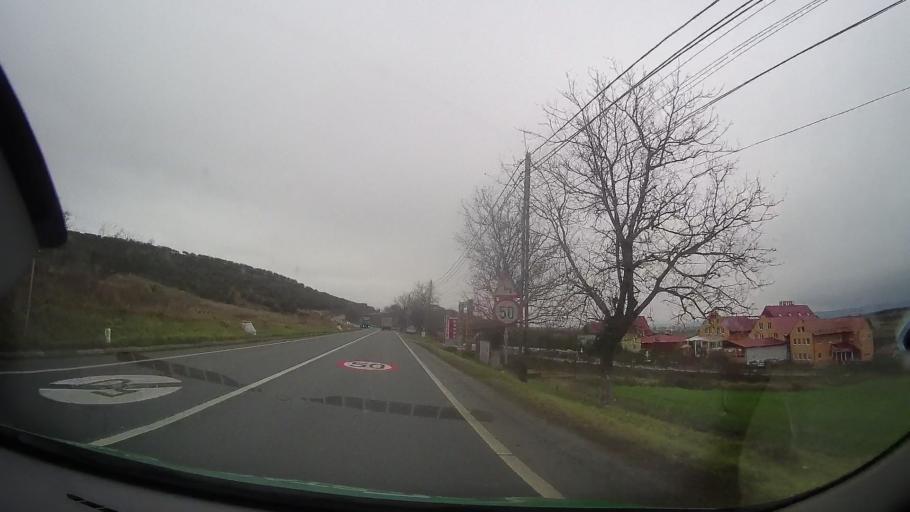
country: RO
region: Mures
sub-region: Comuna Breaza
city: Breaza
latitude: 46.7702
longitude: 24.6576
